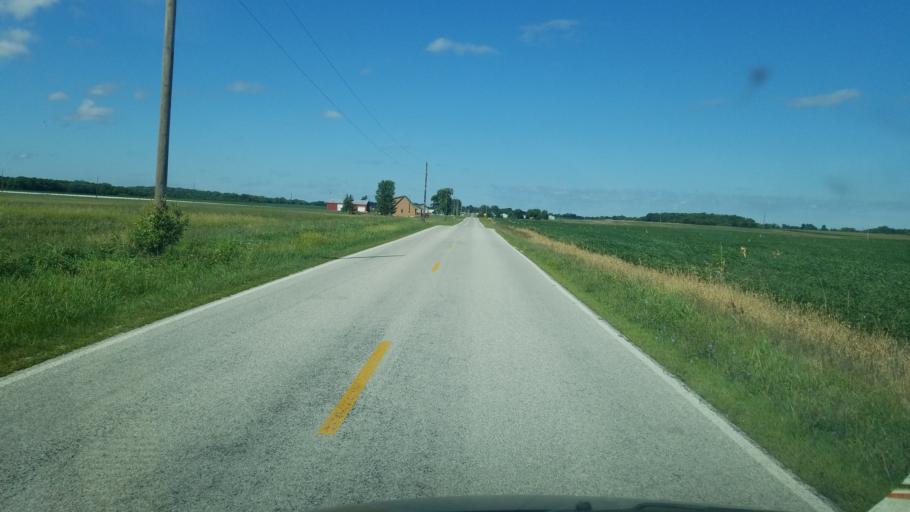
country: US
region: Ohio
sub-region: Wood County
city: North Baltimore
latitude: 41.1241
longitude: -83.6822
